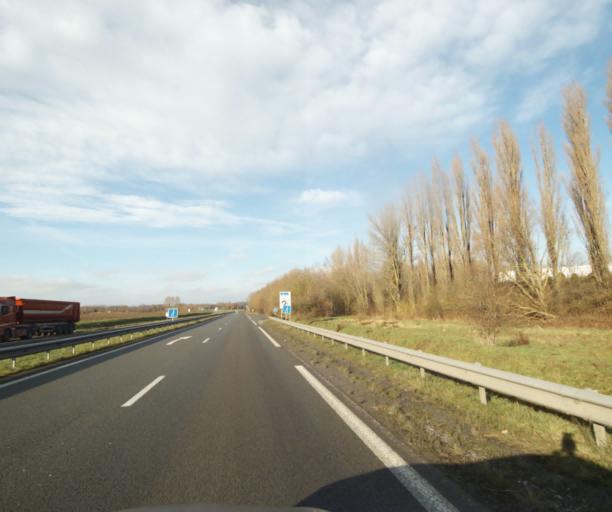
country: FR
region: Nord-Pas-de-Calais
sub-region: Departement du Nord
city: Saultain
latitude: 50.3392
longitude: 3.5864
